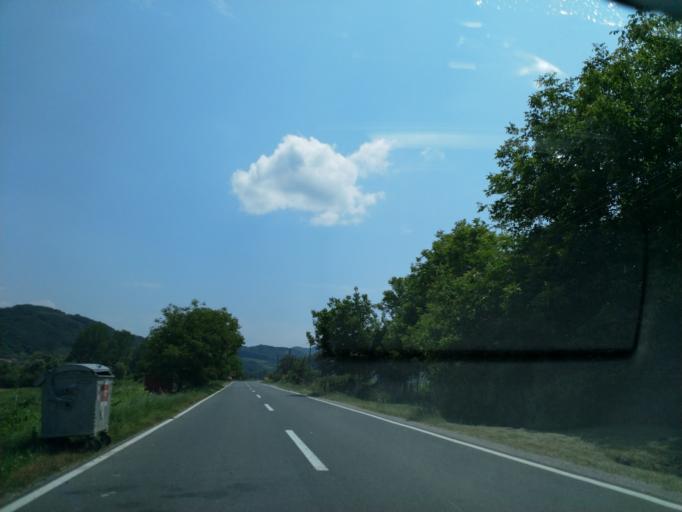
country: RS
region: Central Serbia
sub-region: Rasinski Okrug
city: Aleksandrovac
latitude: 43.3787
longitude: 21.1612
